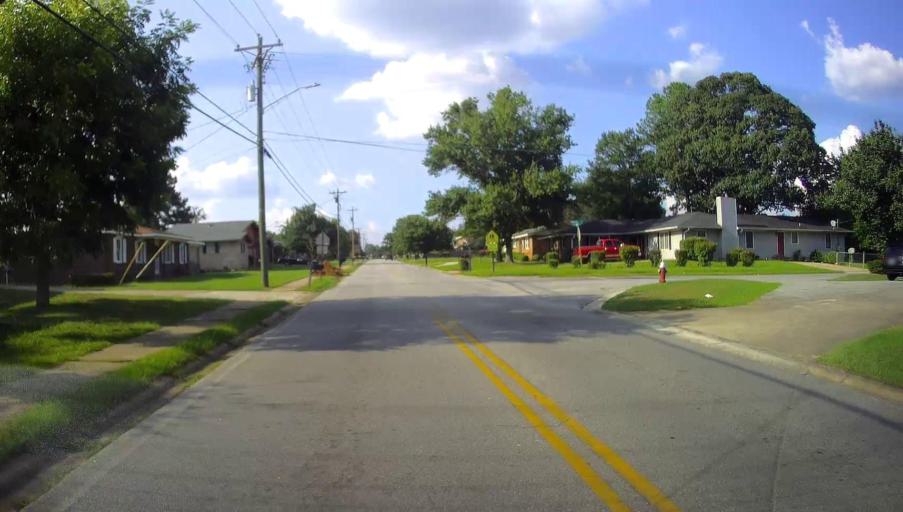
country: US
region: Georgia
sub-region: Houston County
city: Warner Robins
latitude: 32.5949
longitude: -83.6369
